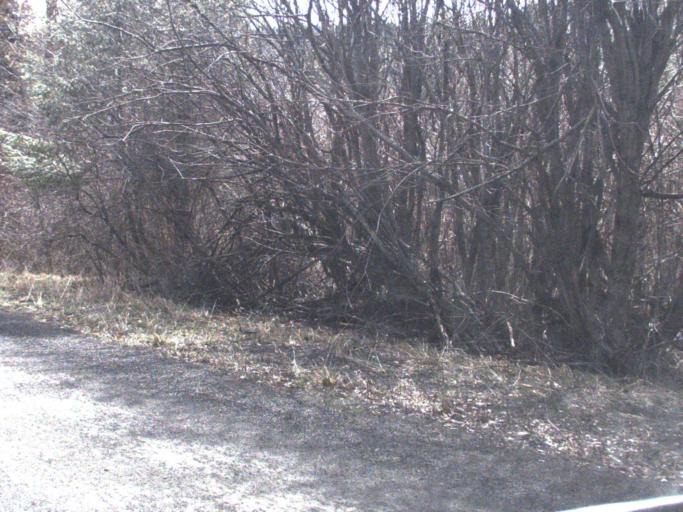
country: US
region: Washington
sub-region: Kittitas County
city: Cle Elum
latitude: 46.9544
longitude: -121.0735
